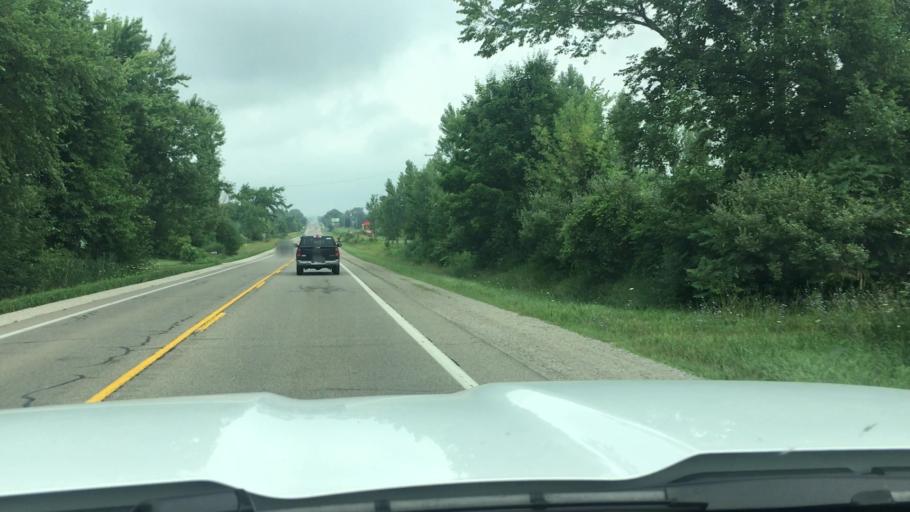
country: US
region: Michigan
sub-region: Sanilac County
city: Brown City
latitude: 43.2004
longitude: -83.0770
